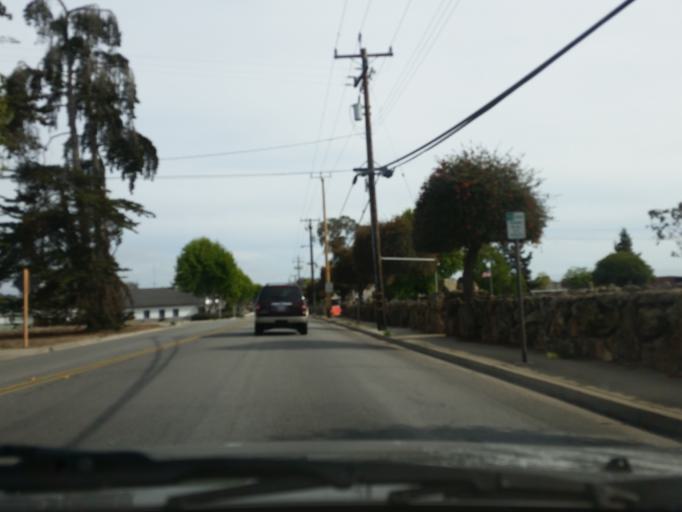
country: US
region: California
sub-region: San Luis Obispo County
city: Arroyo Grande
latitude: 35.1227
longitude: -120.5916
